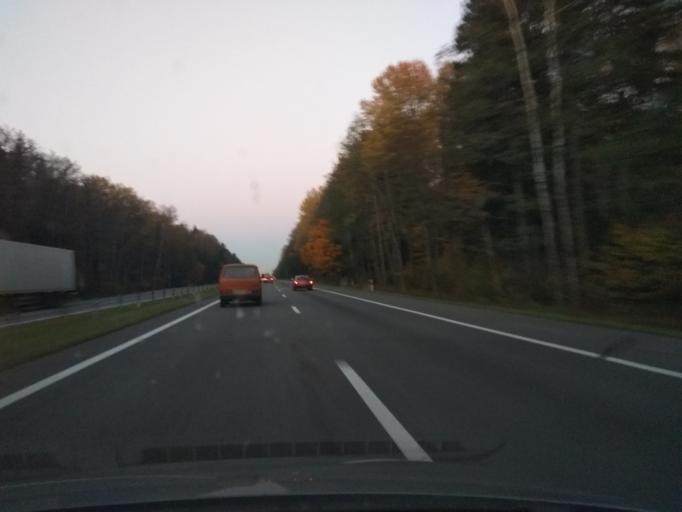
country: BY
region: Minsk
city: Enyerhyetykaw
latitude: 53.5754
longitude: 27.0113
